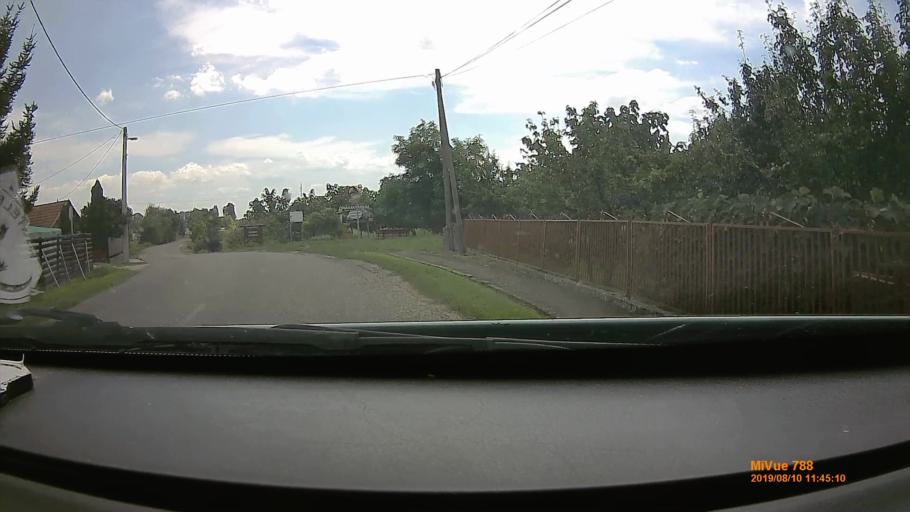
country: HU
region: Borsod-Abauj-Zemplen
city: Szentistvan
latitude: 47.7184
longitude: 20.6257
